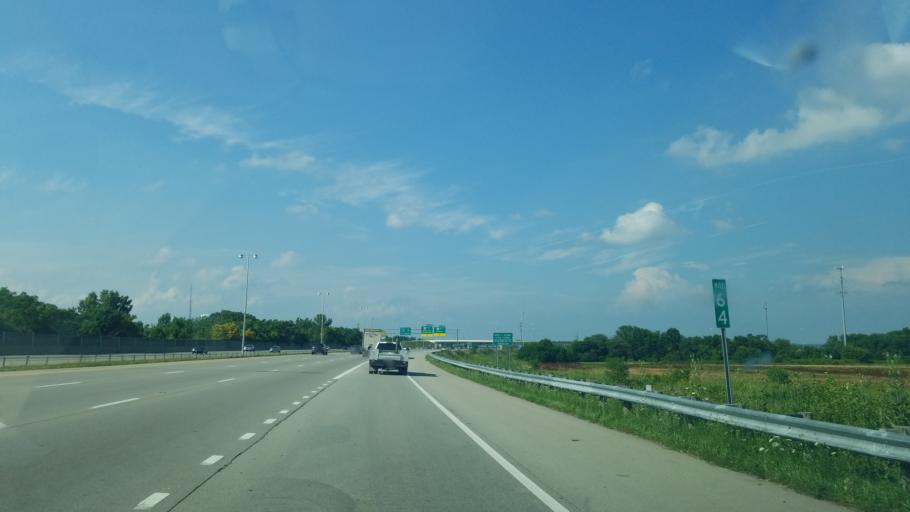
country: US
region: Ohio
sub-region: Clermont County
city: Summerside
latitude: 39.0940
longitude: -84.2883
